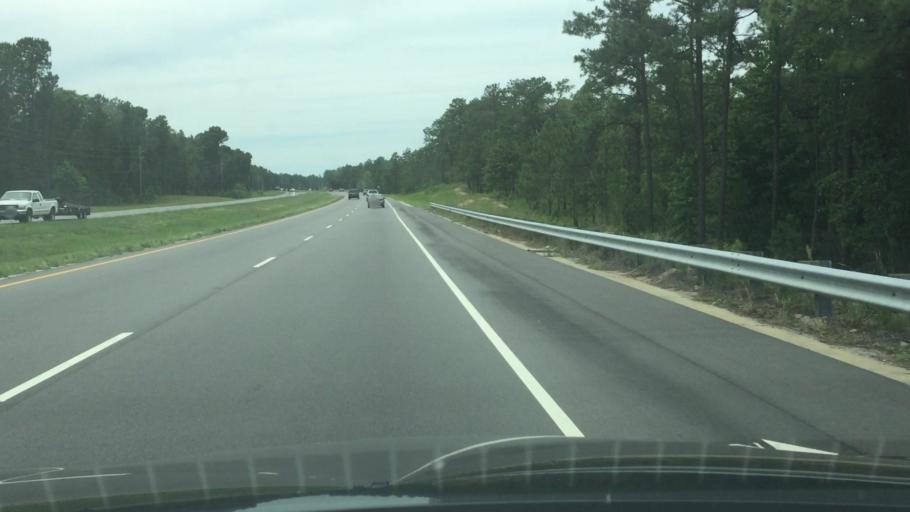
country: US
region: North Carolina
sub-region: Cumberland County
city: Spring Lake
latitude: 35.2254
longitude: -79.0093
